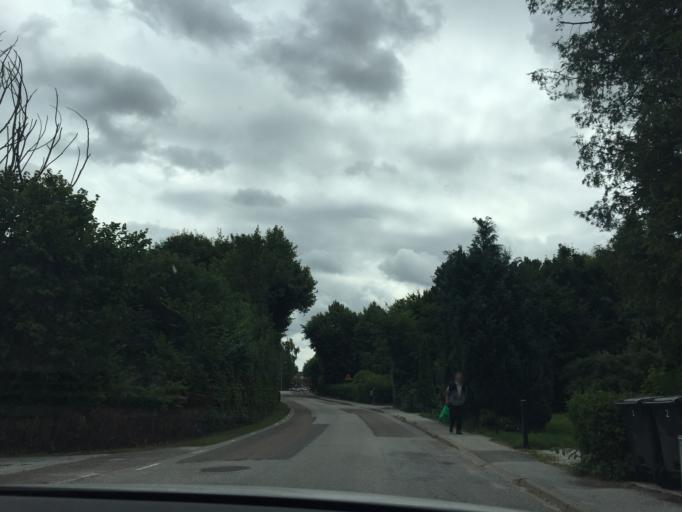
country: SE
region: Skane
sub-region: Sjobo Kommun
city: Blentarp
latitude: 55.5862
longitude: 13.6005
